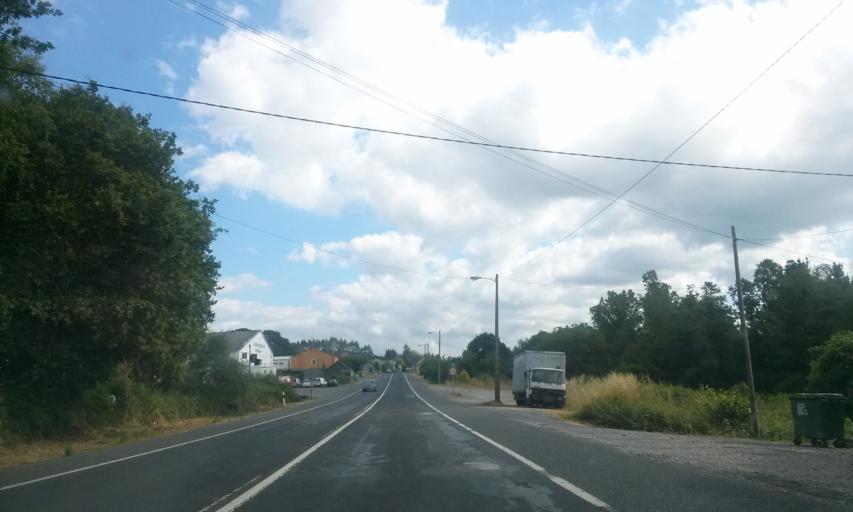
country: ES
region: Galicia
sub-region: Provincia de Lugo
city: Outeiro de Rei
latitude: 43.0896
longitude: -7.6064
